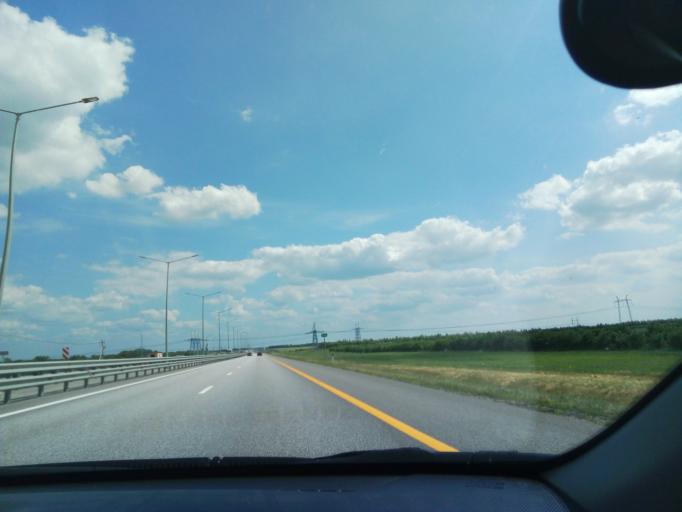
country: RU
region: Voronezj
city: Podkletnoye
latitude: 51.5546
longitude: 39.4877
